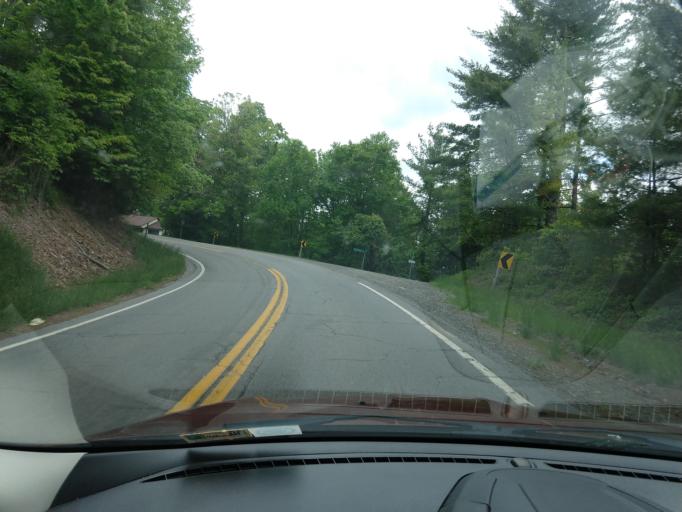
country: US
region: Virginia
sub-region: City of Galax
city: Galax
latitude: 36.7734
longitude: -80.9831
